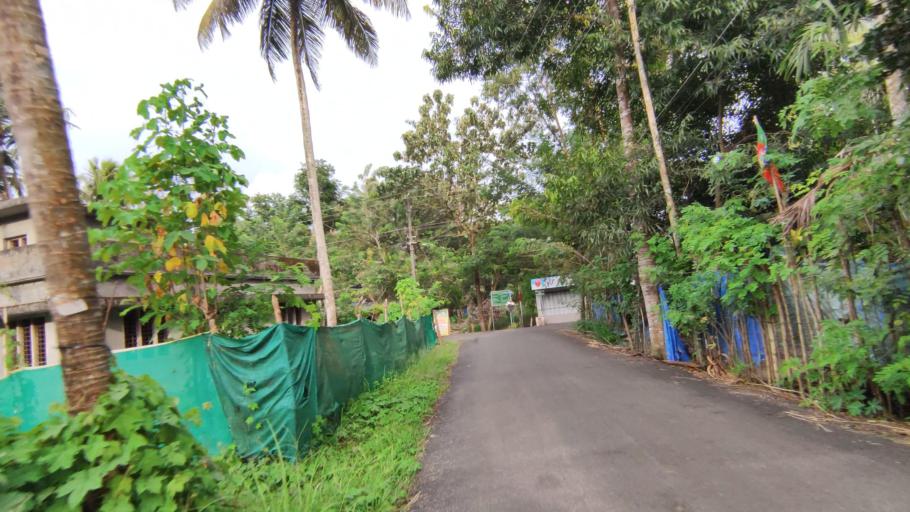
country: IN
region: Kerala
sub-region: Alappuzha
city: Shertallai
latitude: 9.6199
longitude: 76.3417
